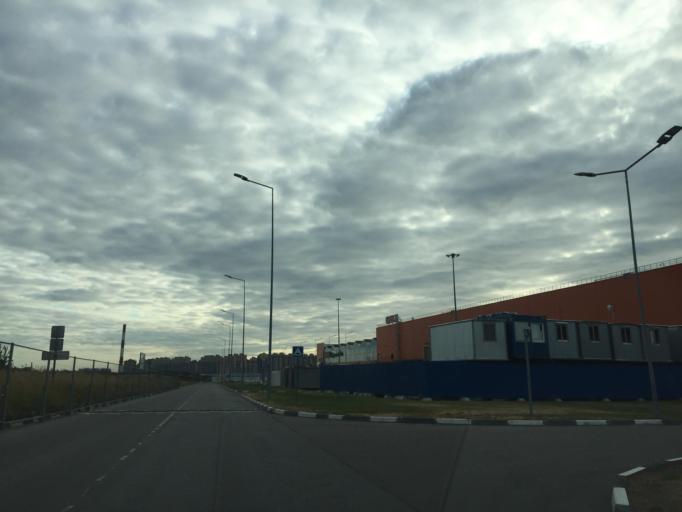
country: RU
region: Leningrad
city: Bugry
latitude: 60.0898
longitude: 30.3850
